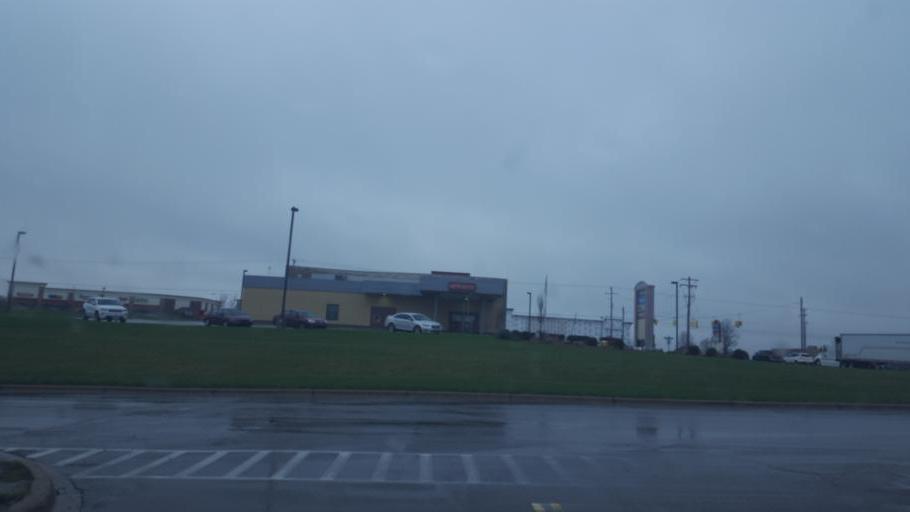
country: US
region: Michigan
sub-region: Isabella County
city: Mount Pleasant
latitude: 43.5742
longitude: -84.7582
